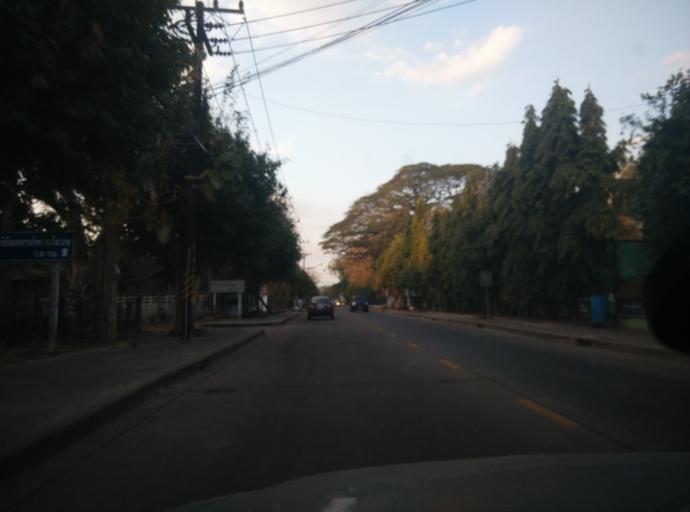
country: TH
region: Sisaket
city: Si Sa Ket
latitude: 15.1186
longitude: 104.3201
